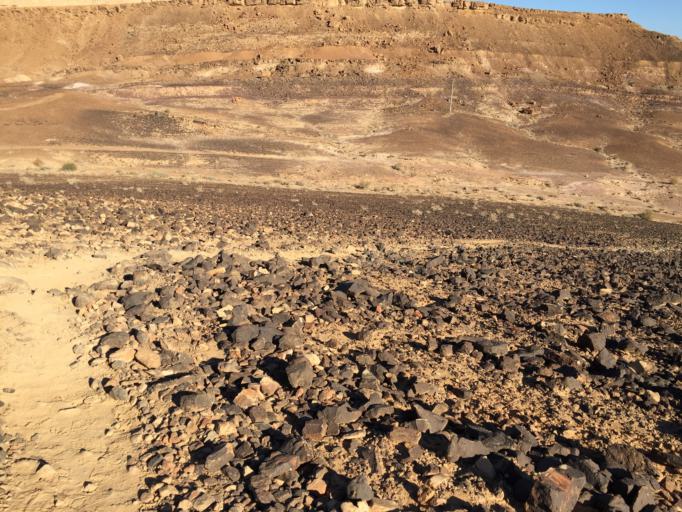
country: IL
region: Southern District
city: Mitzpe Ramon
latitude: 30.6161
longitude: 34.8389
